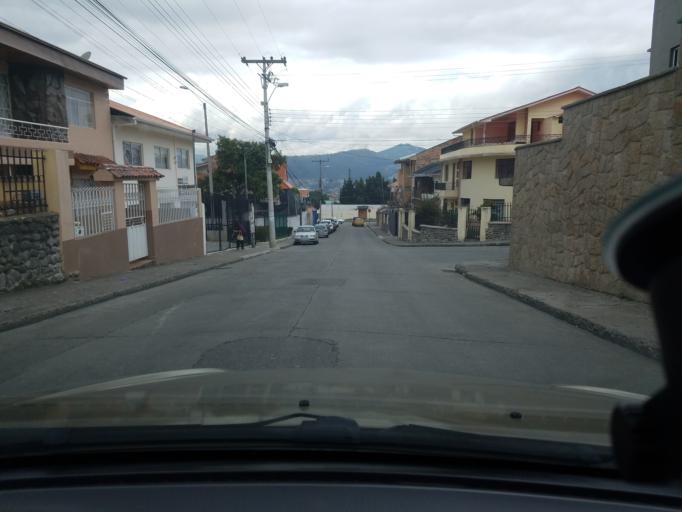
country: EC
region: Azuay
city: Cuenca
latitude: -2.8878
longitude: -79.0006
